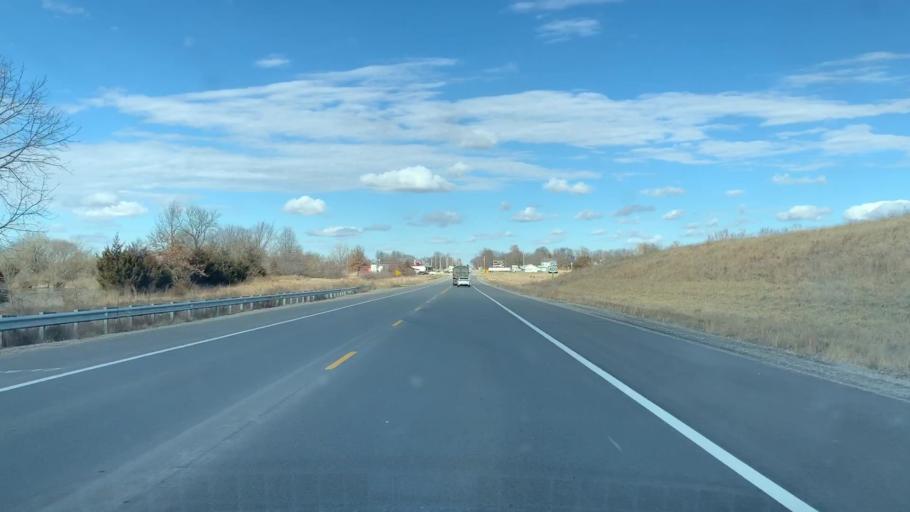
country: US
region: Kansas
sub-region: Crawford County
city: Pittsburg
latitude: 37.3354
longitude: -94.8321
